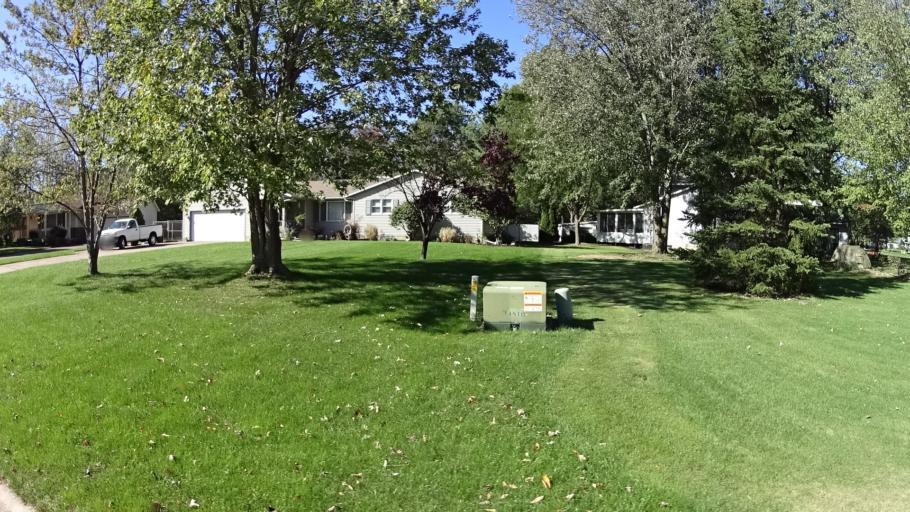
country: US
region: Ohio
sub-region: Lorain County
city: Amherst
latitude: 41.3958
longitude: -82.1933
